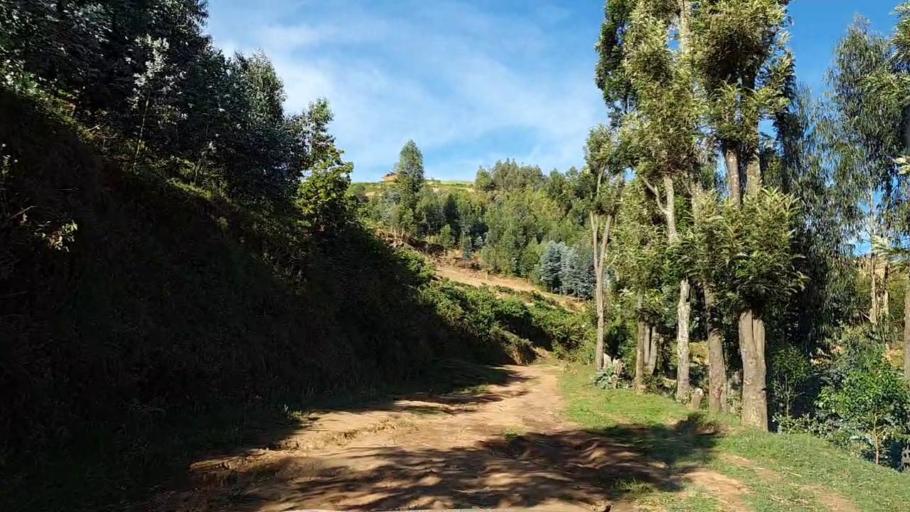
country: RW
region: Southern Province
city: Gikongoro
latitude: -2.4135
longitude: 29.5166
